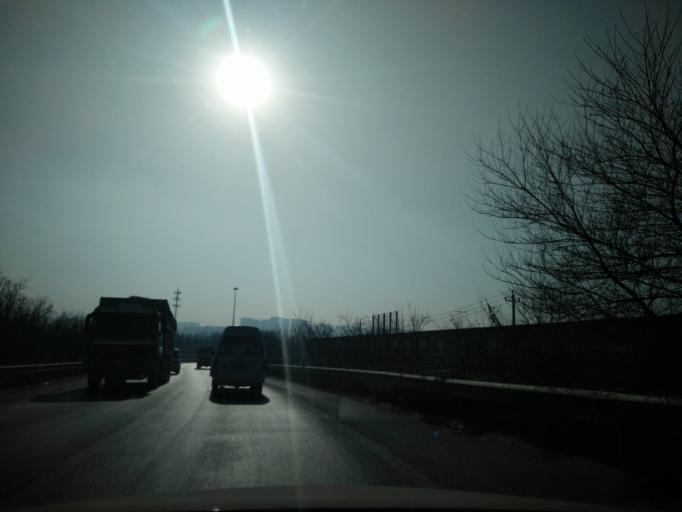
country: CN
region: Beijing
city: Jiugong
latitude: 39.8198
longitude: 116.4957
